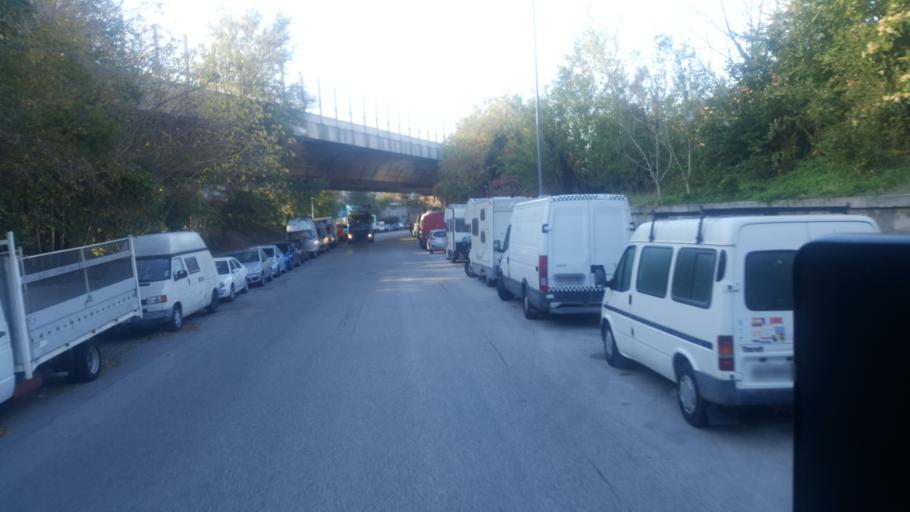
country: IT
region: Friuli Venezia Giulia
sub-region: Provincia di Trieste
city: Trieste
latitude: 45.6385
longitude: 13.7719
